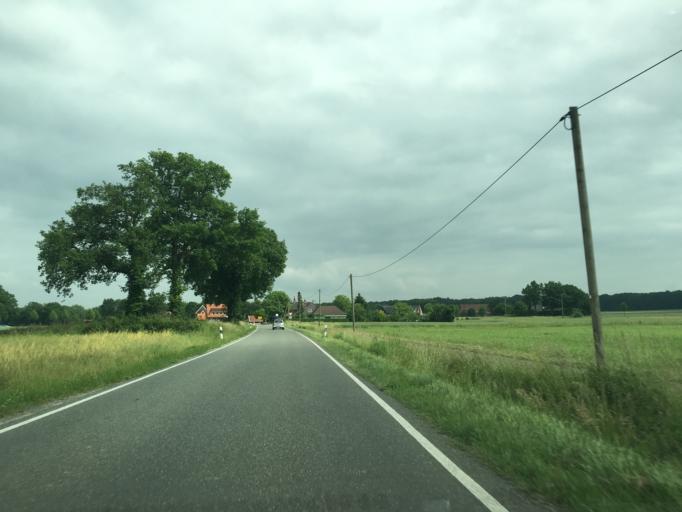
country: DE
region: North Rhine-Westphalia
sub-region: Regierungsbezirk Munster
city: Horstmar
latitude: 52.0992
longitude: 7.3212
